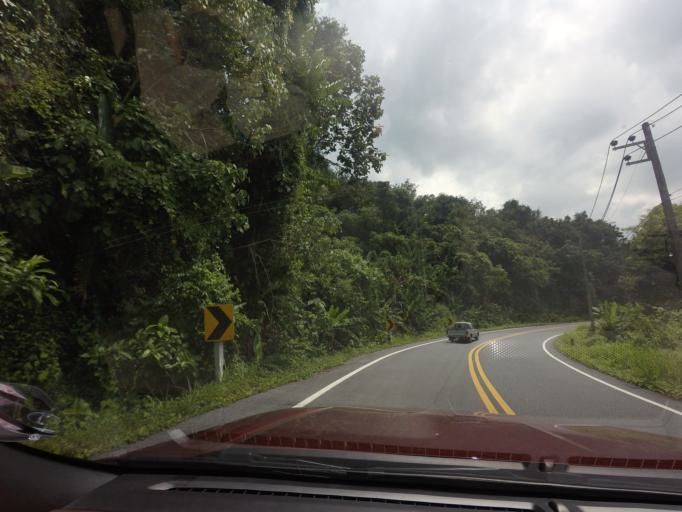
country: TH
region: Yala
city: Than To
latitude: 6.0361
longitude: 101.2055
